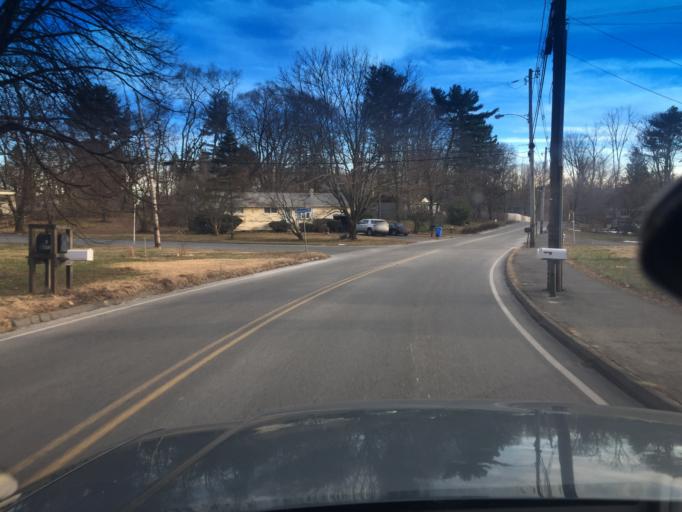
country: US
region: Massachusetts
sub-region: Middlesex County
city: Holliston
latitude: 42.2119
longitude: -71.4186
